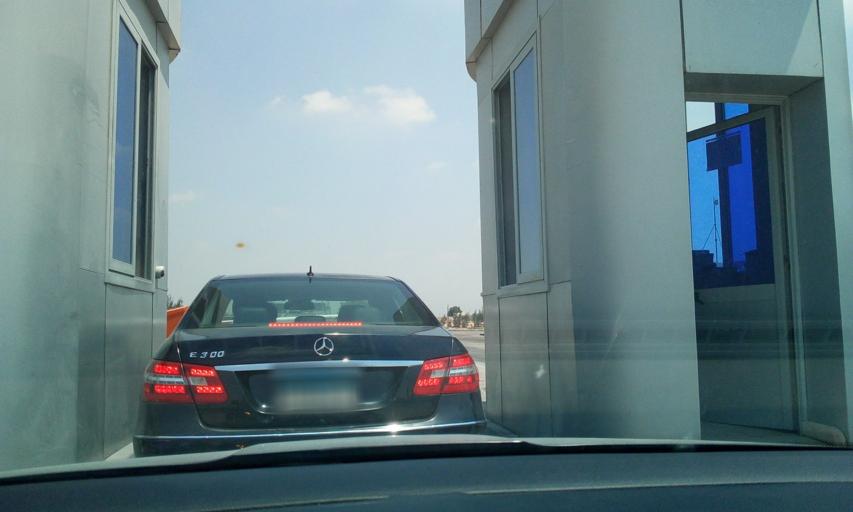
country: EG
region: Al Buhayrah
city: Beheira
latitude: 30.5128
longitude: 30.2215
